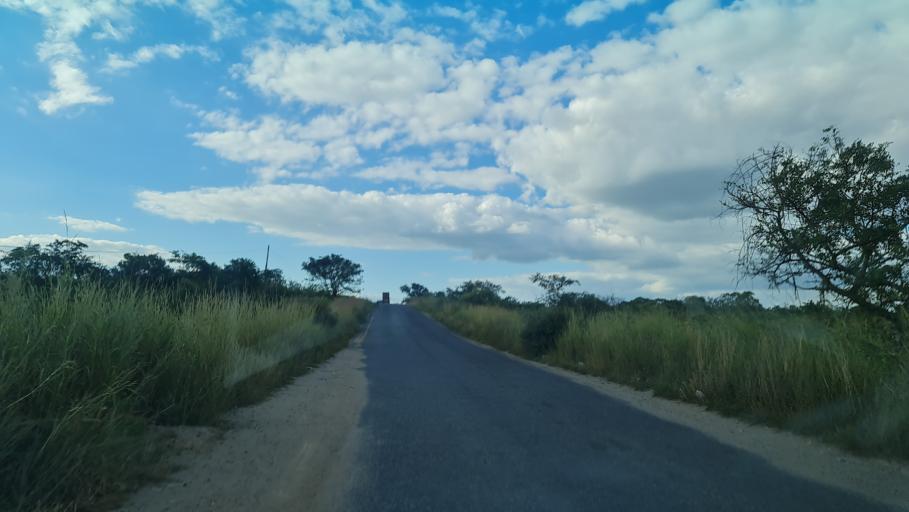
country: MZ
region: Manica
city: Chimoio
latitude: -19.2227
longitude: 33.9207
